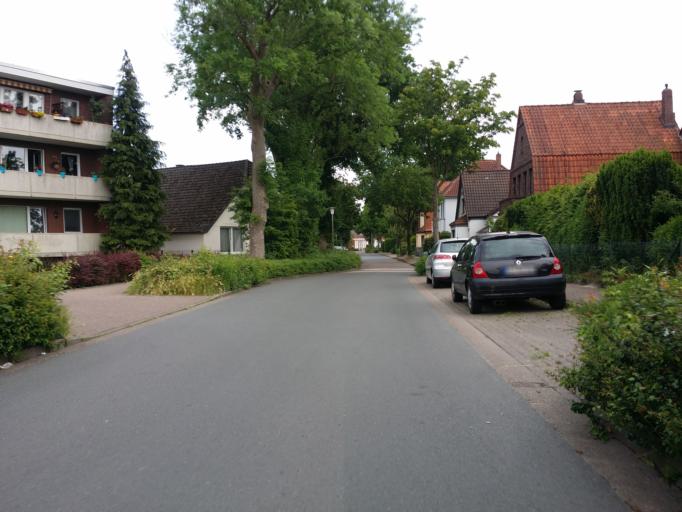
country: DE
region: Lower Saxony
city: Oldenburg
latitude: 53.1554
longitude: 8.2260
